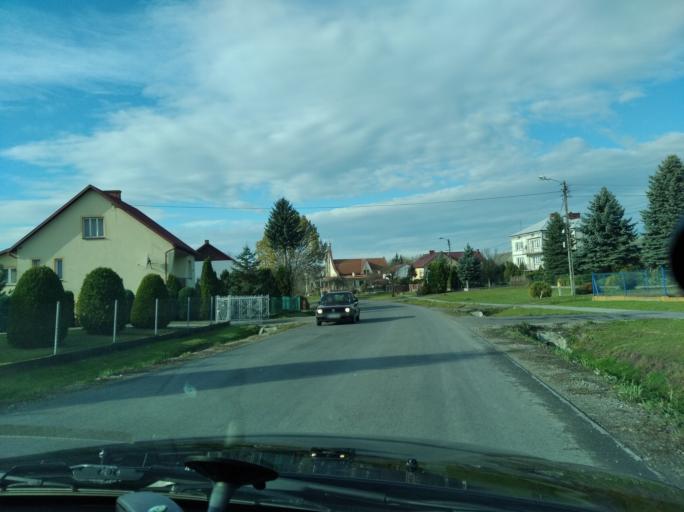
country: PL
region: Subcarpathian Voivodeship
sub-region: Powiat ropczycko-sedziszowski
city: Sedziszow Malopolski
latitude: 50.0786
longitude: 21.7399
